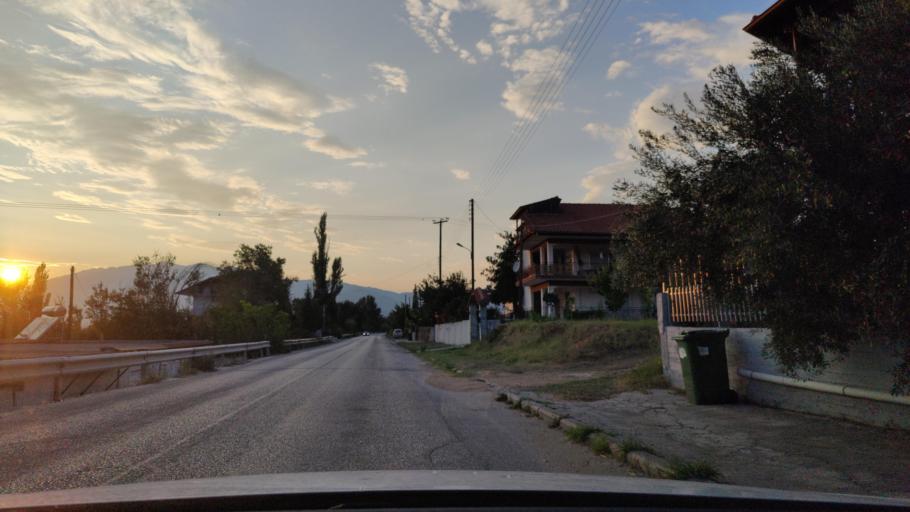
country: GR
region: Central Macedonia
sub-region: Nomos Serron
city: Sidirokastro
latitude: 41.2432
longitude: 23.3833
